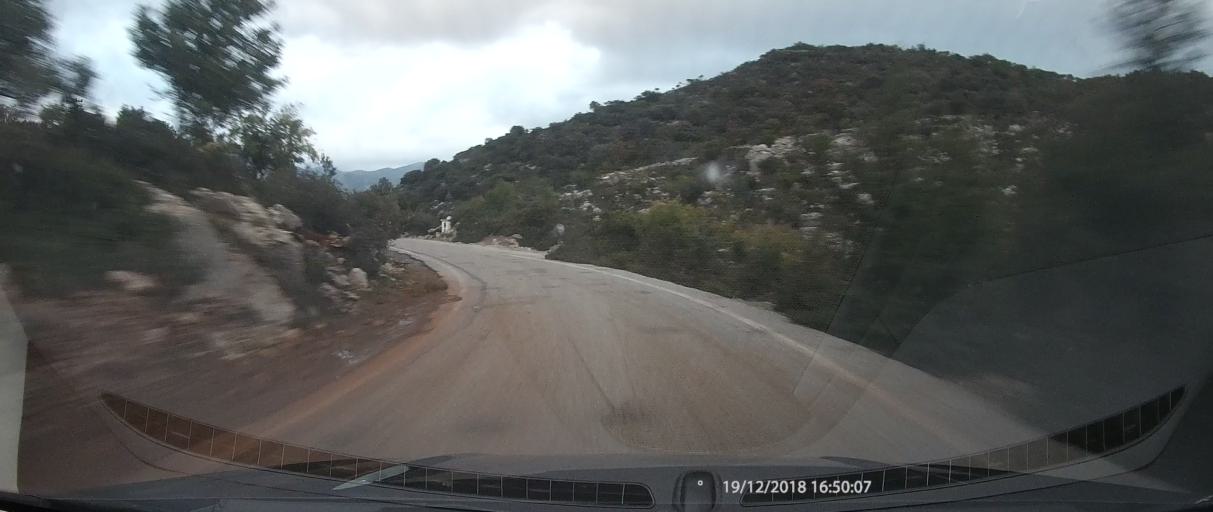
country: GR
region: Peloponnese
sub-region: Nomos Lakonias
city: Sykea
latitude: 36.9506
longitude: 22.9961
